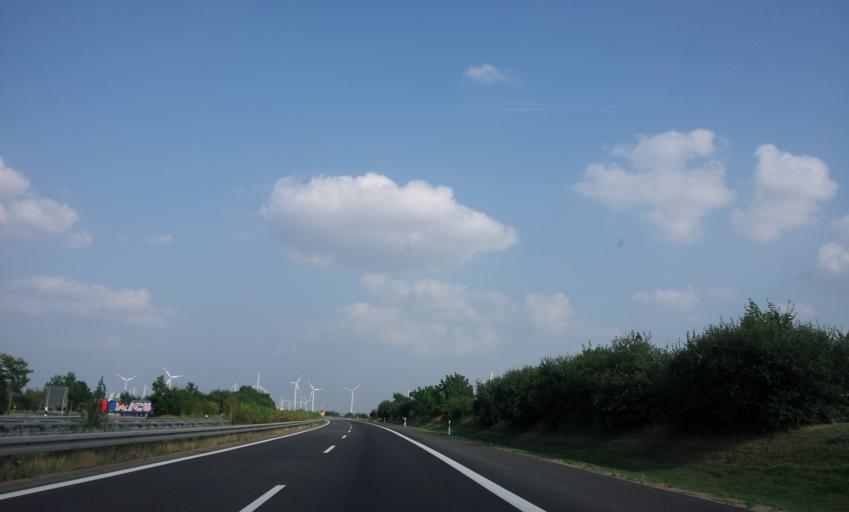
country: DE
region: Mecklenburg-Vorpommern
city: Strasburg
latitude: 53.5212
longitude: 13.7759
